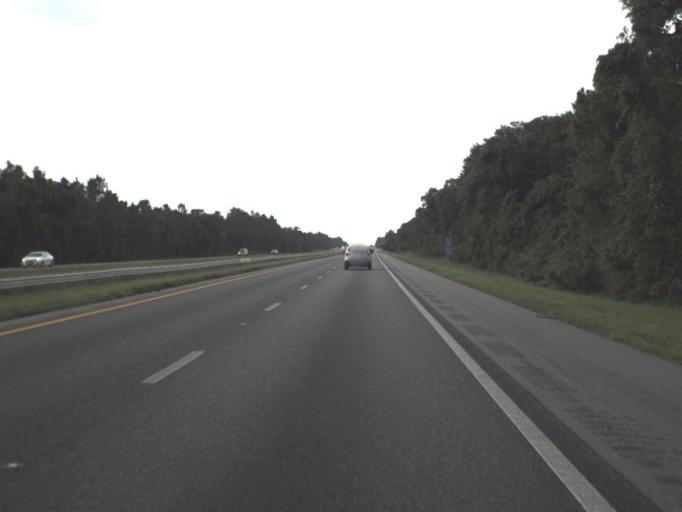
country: US
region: Florida
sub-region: Hernando County
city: Hill 'n Dale
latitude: 28.5526
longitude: -82.2371
